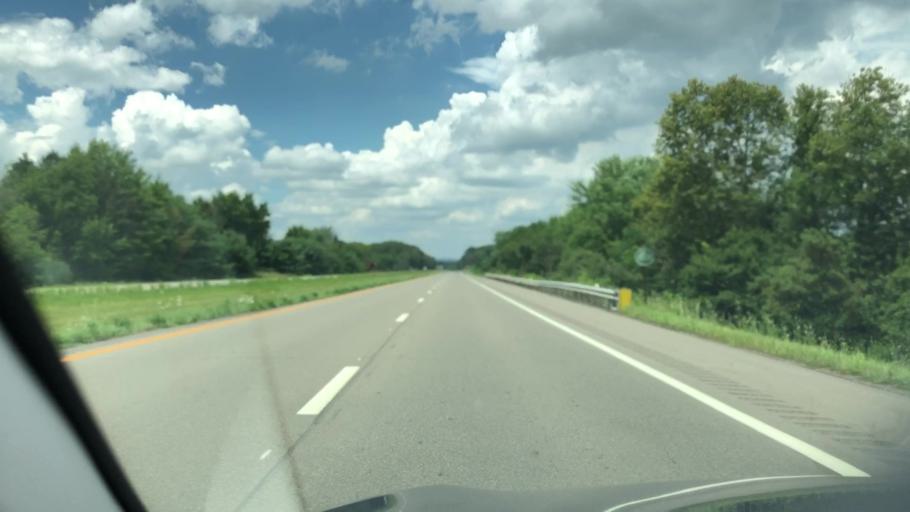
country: US
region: Ohio
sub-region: Stark County
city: Massillon
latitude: 40.8321
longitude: -81.5462
